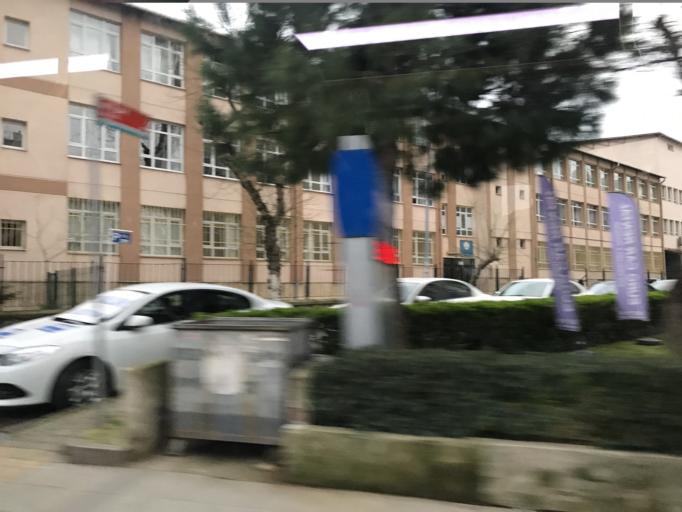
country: TR
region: Istanbul
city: UEskuedar
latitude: 40.9837
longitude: 29.0604
